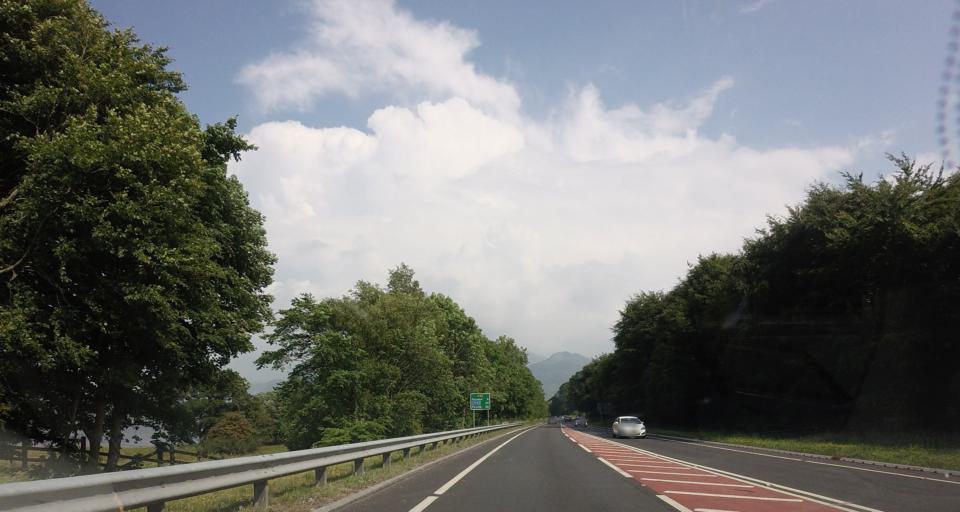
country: GB
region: England
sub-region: Cumbria
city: Cockermouth
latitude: 54.6680
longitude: -3.2435
